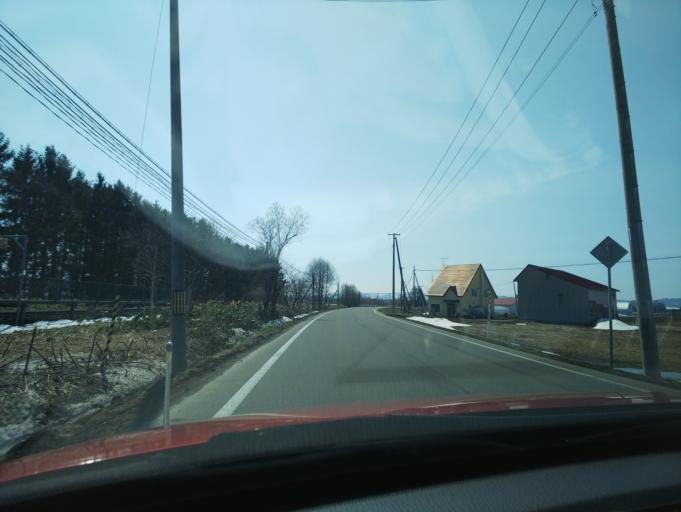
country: JP
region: Hokkaido
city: Nayoro
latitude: 44.3174
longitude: 142.4635
